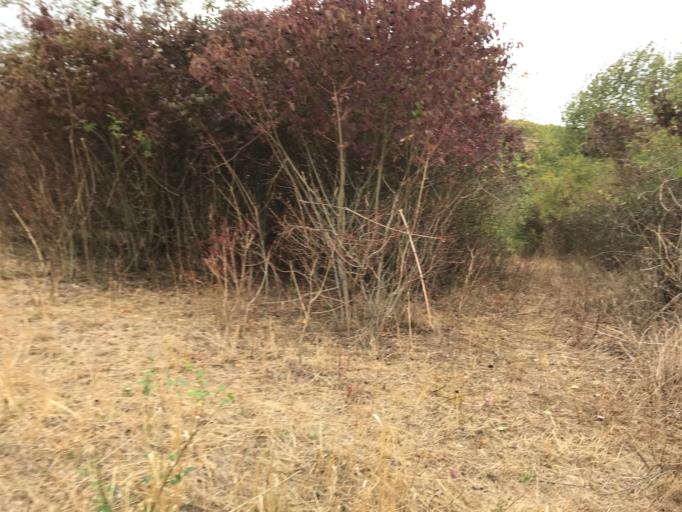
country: DE
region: Rheinland-Pfalz
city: Jugenheim
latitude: 49.9032
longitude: 8.1016
